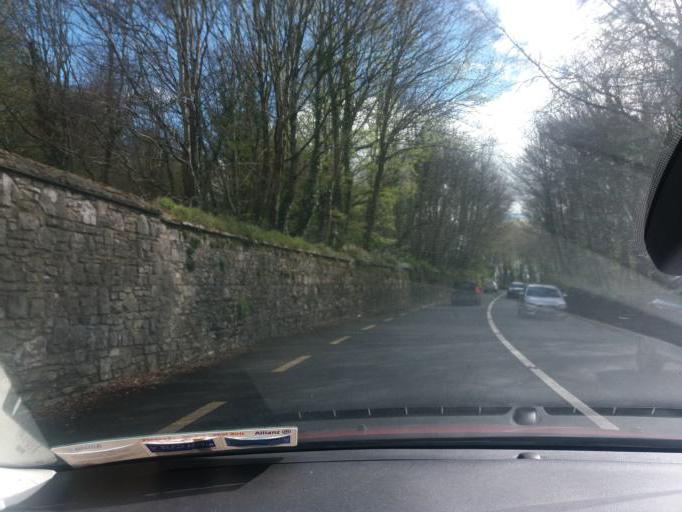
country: IE
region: Munster
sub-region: County Cork
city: Carrigtwohill
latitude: 51.8943
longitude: -8.2851
